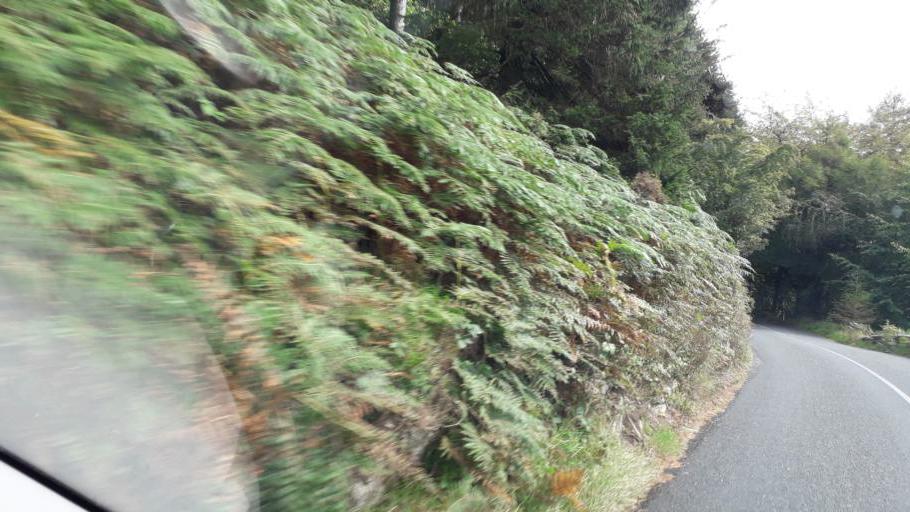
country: IE
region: Leinster
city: Ballinteer
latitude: 53.2315
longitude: -6.2734
